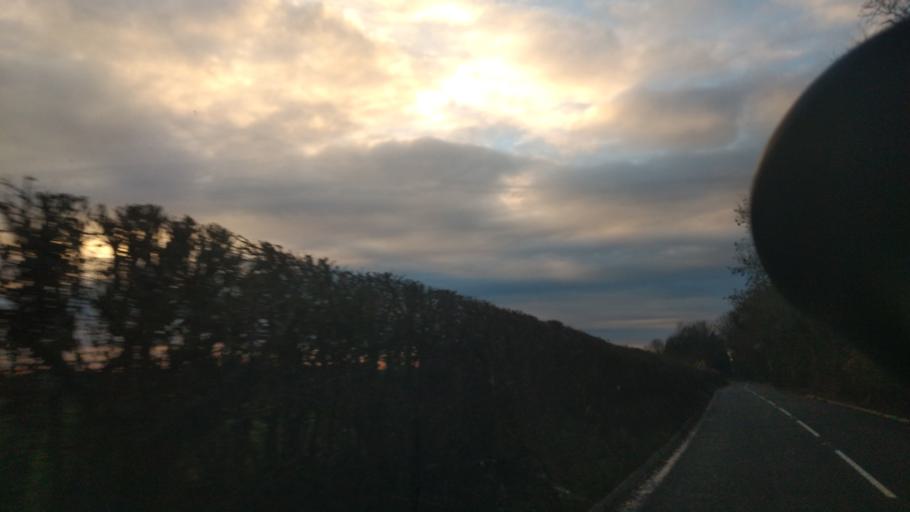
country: GB
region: England
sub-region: Wiltshire
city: Westwood
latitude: 51.3272
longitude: -2.2583
